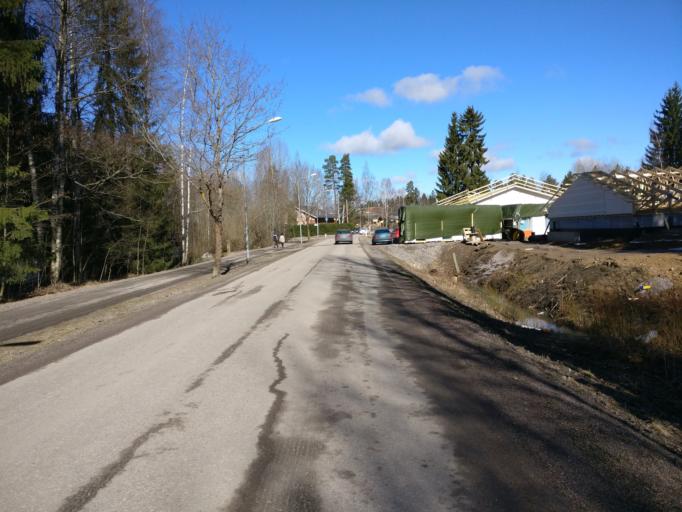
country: FI
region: Uusimaa
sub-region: Helsinki
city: Jaervenpaeae
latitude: 60.4913
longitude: 25.0800
